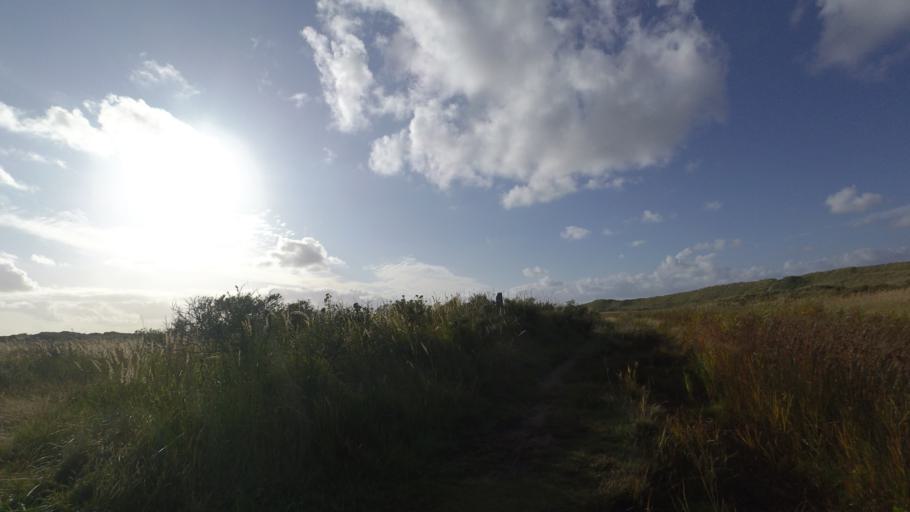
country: NL
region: Friesland
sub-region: Gemeente Dongeradeel
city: Ternaard
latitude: 53.4644
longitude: 5.9138
